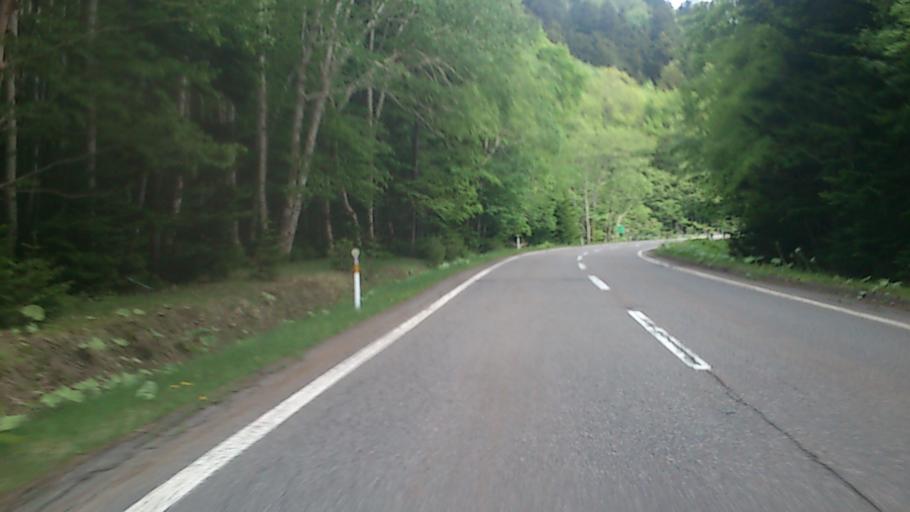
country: JP
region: Hokkaido
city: Kitami
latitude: 43.4001
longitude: 143.9856
